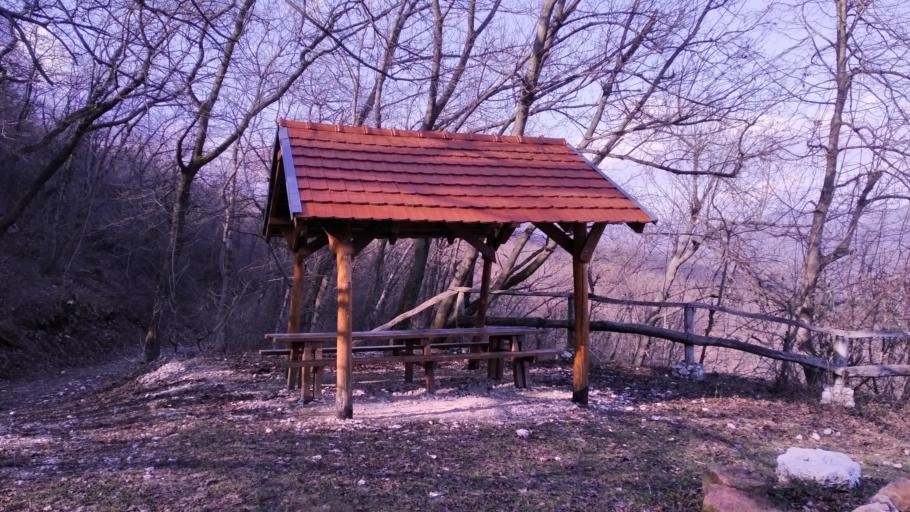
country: HU
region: Pest
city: Pilisborosjeno
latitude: 47.6239
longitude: 18.9928
